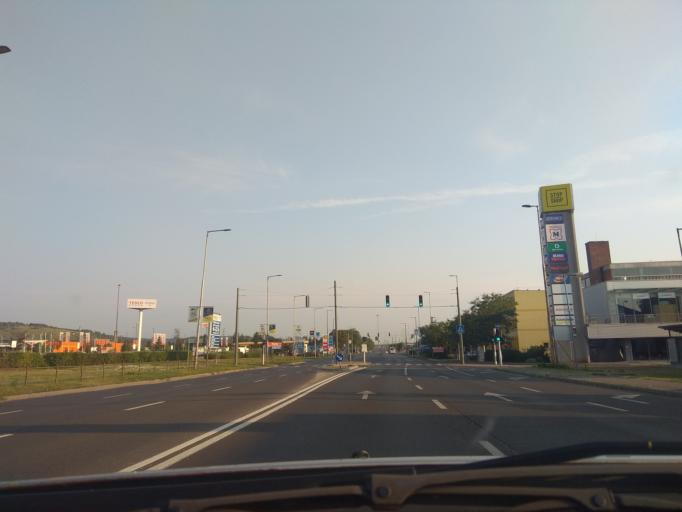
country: HU
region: Borsod-Abauj-Zemplen
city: Miskolc
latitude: 48.1265
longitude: 20.7847
